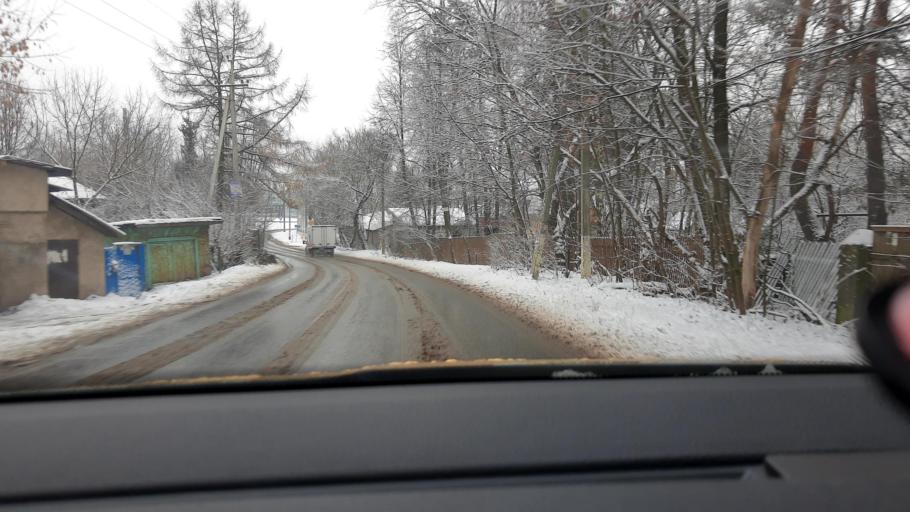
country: RU
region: Moskovskaya
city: Mamontovka
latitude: 55.9672
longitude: 37.8330
